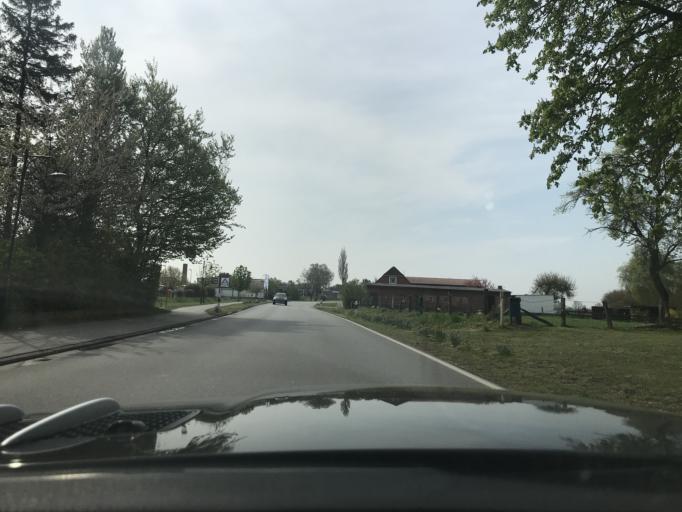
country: DE
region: Schleswig-Holstein
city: Grube
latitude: 54.2250
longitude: 11.0343
